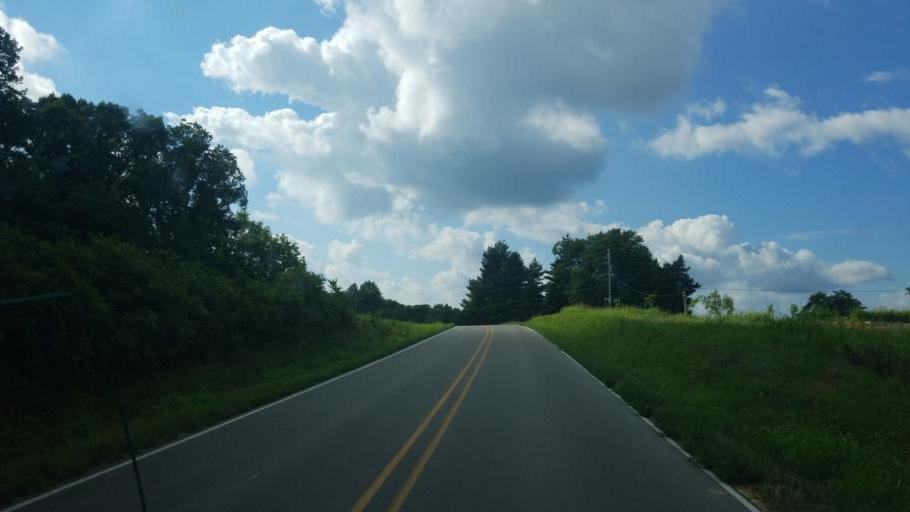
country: US
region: Illinois
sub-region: Union County
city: Cobden
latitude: 37.5553
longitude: -89.2968
